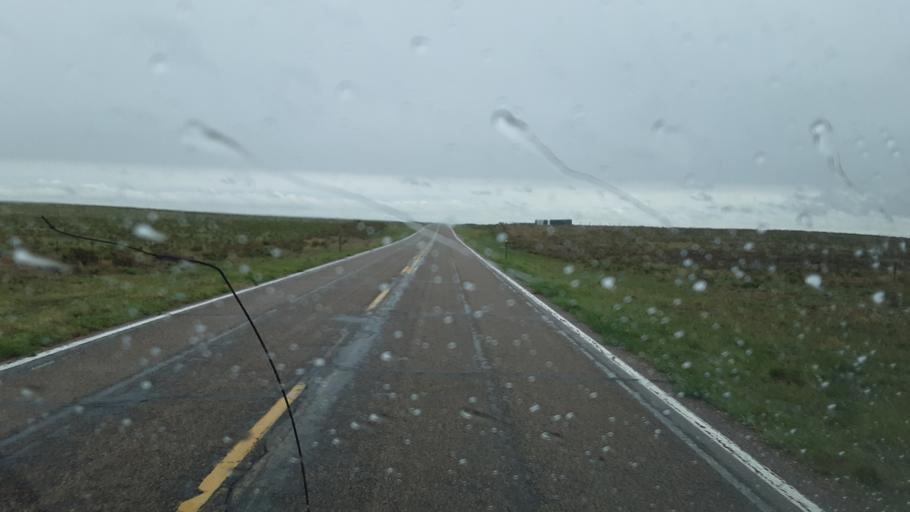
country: US
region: Colorado
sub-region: Lincoln County
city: Hugo
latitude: 38.8496
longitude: -103.1794
